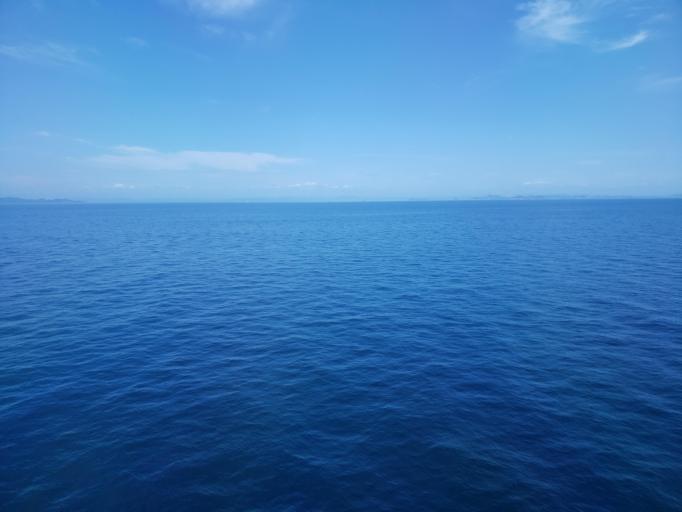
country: JP
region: Tokushima
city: Narutocho-mitsuishi
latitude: 34.4660
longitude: 134.4824
